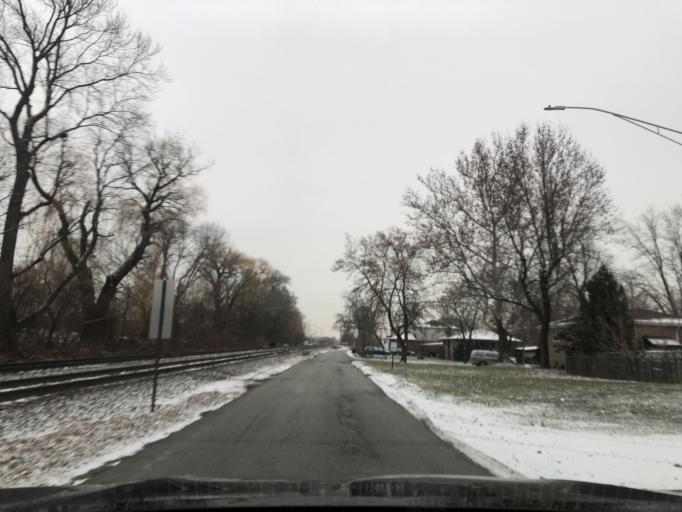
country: US
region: Illinois
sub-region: Cook County
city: Evergreen Park
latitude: 41.7307
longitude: -87.6874
